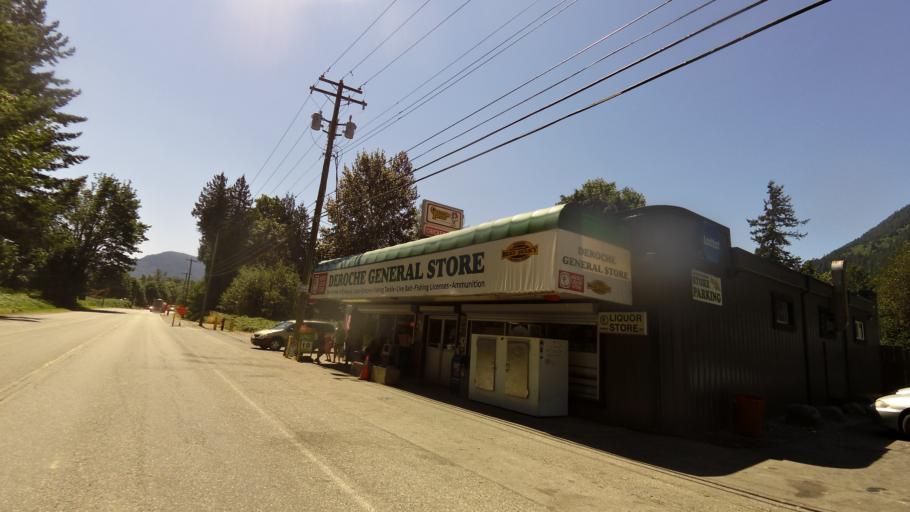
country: CA
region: British Columbia
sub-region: Fraser Valley Regional District
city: Chilliwack
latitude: 49.1899
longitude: -122.0713
